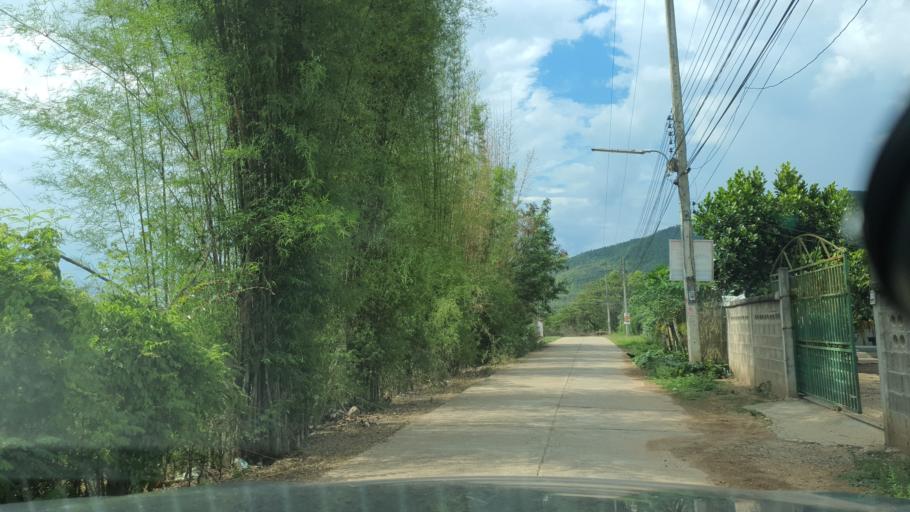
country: TH
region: Chiang Mai
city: Mae Taeng
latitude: 19.1409
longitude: 99.0373
